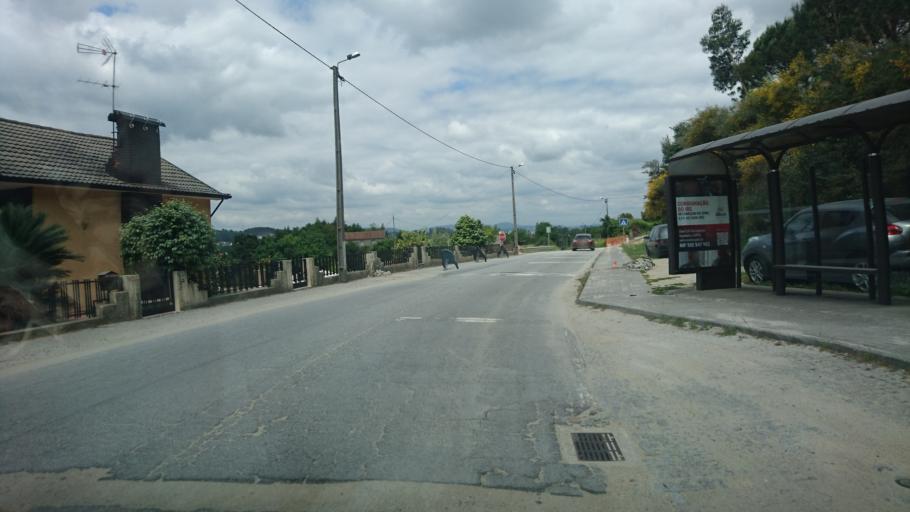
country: PT
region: Porto
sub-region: Paredes
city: Baltar
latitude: 41.1603
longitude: -8.3574
